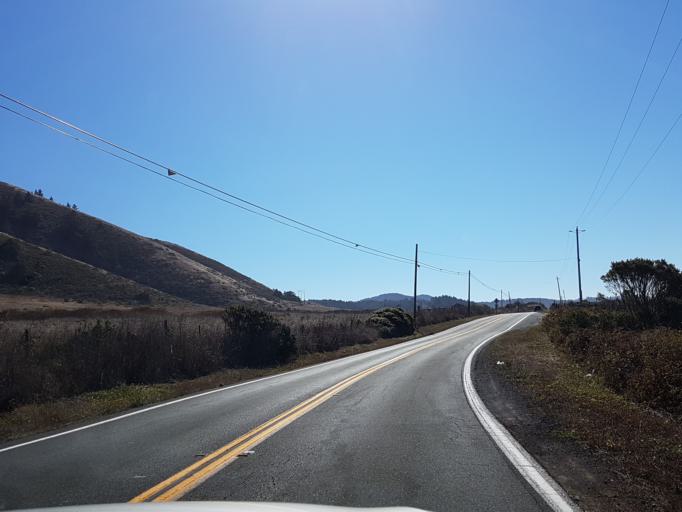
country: US
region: California
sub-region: Mendocino County
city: Boonville
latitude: 39.0744
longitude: -123.6939
